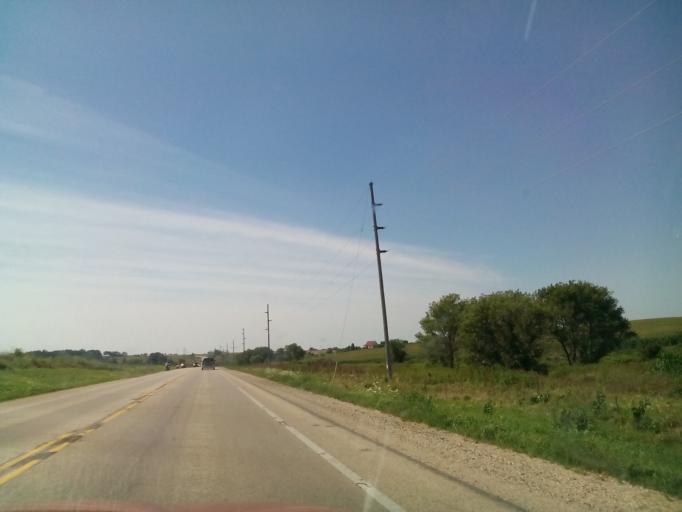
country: US
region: Wisconsin
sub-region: Green County
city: Monroe
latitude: 42.6655
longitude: -89.6218
